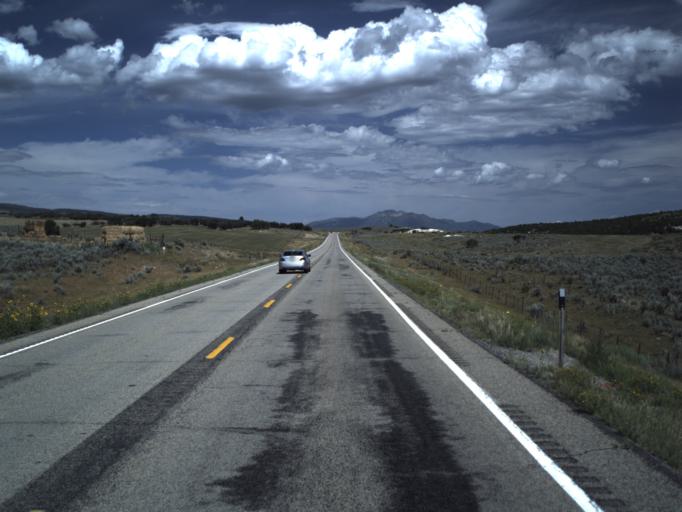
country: US
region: Utah
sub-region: Sanpete County
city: Fairview
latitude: 39.6961
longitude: -111.4629
